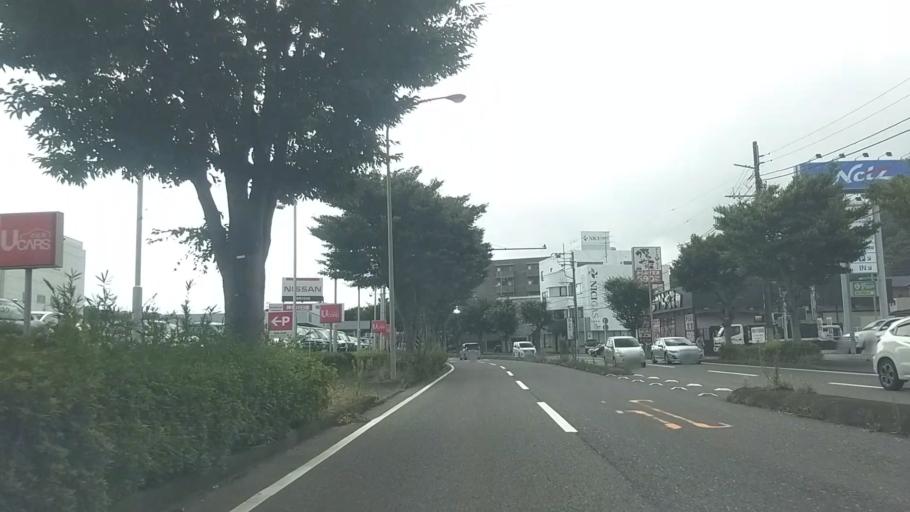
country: JP
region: Kanagawa
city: Yokosuka
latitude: 35.2441
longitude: 139.6824
